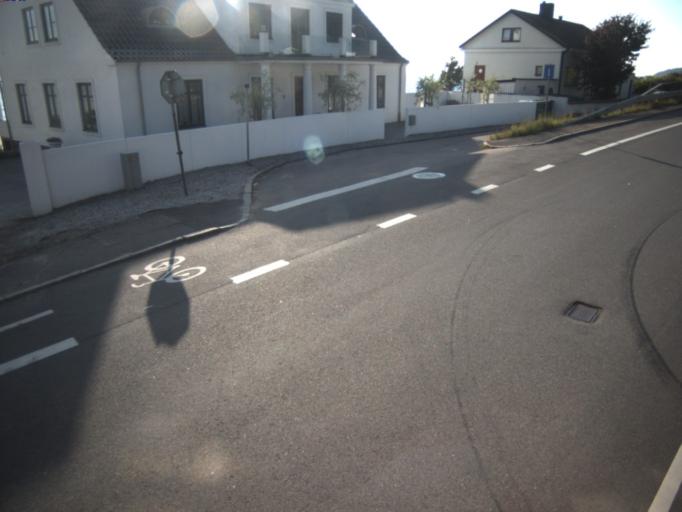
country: SE
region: Skane
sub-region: Helsingborg
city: Helsingborg
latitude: 56.0740
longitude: 12.6671
